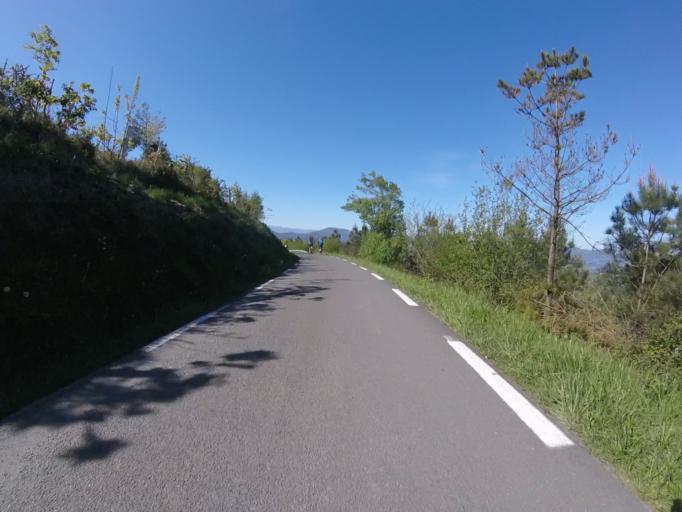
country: ES
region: Basque Country
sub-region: Provincia de Guipuzcoa
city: Errezil
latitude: 43.1896
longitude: -2.2062
